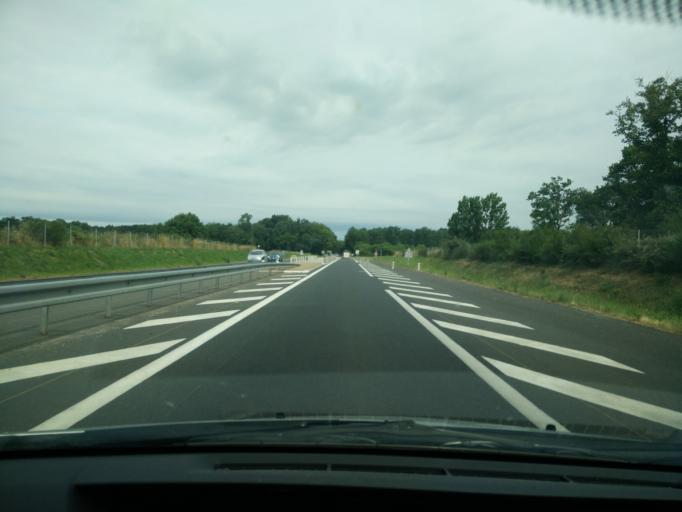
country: FR
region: Pays de la Loire
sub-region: Departement de Maine-et-Loire
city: Saint-Jean
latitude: 47.3048
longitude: -0.3927
